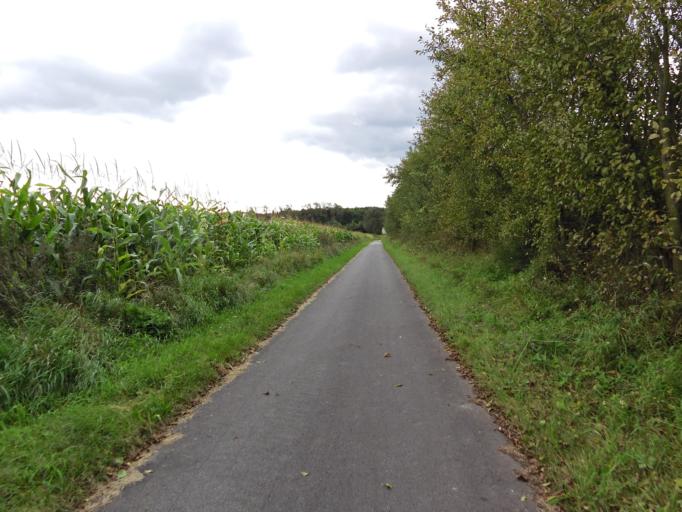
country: DE
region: Saxony-Anhalt
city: Arneburg
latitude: 52.6220
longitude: 12.0009
